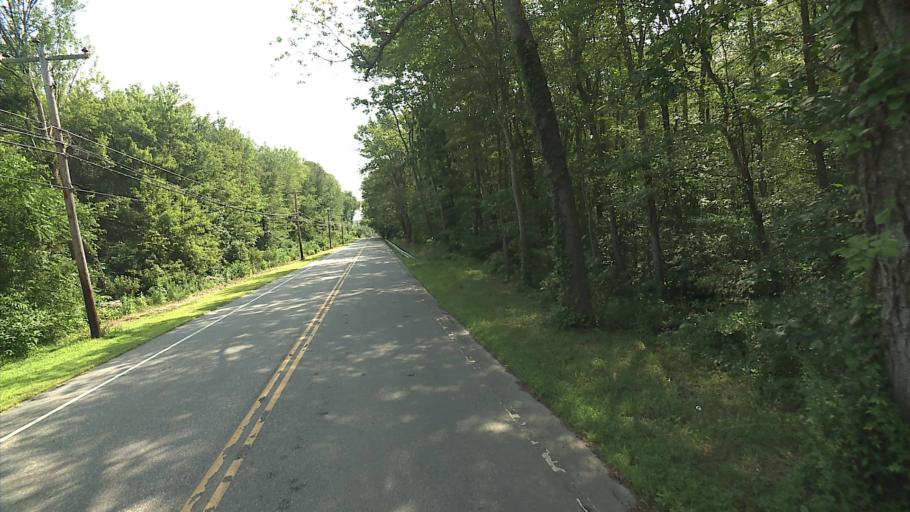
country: US
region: Connecticut
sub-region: New London County
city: Colchester
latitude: 41.5730
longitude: -72.2192
